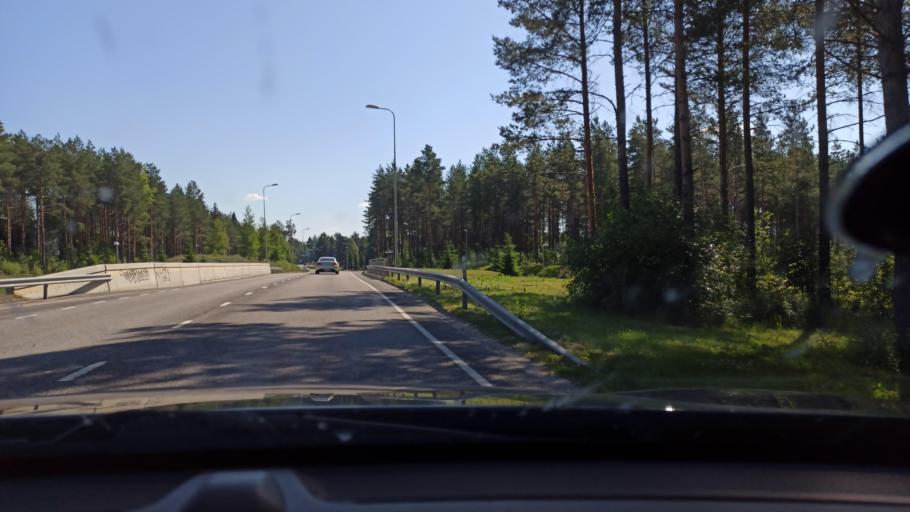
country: FI
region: Northern Ostrobothnia
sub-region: Oulu
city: Oulu
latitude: 65.0401
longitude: 25.4595
